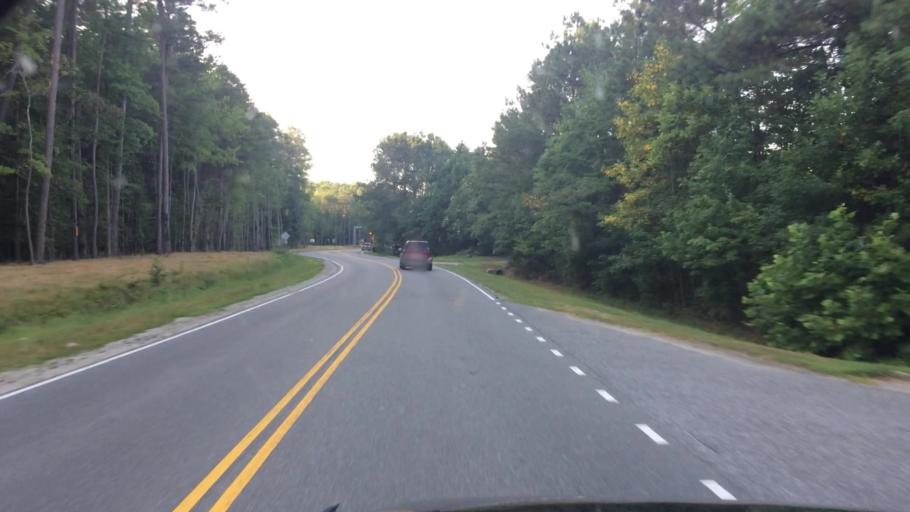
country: US
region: Virginia
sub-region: James City County
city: Williamsburg
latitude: 37.3152
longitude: -76.7306
